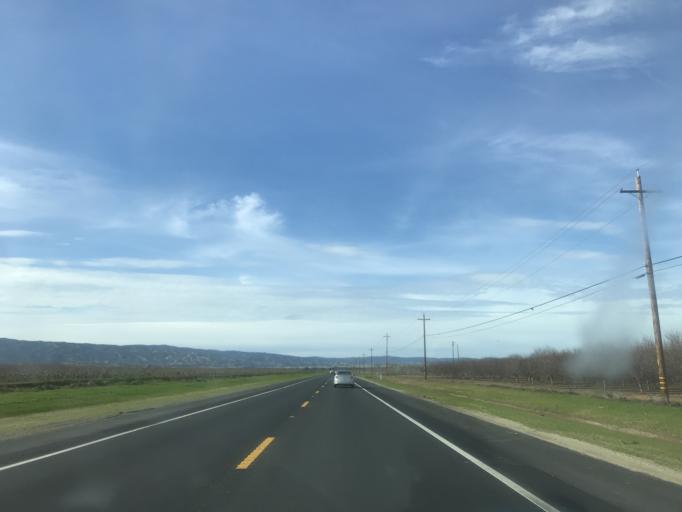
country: US
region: California
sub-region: Yolo County
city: Cottonwood
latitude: 38.6831
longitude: -121.9760
